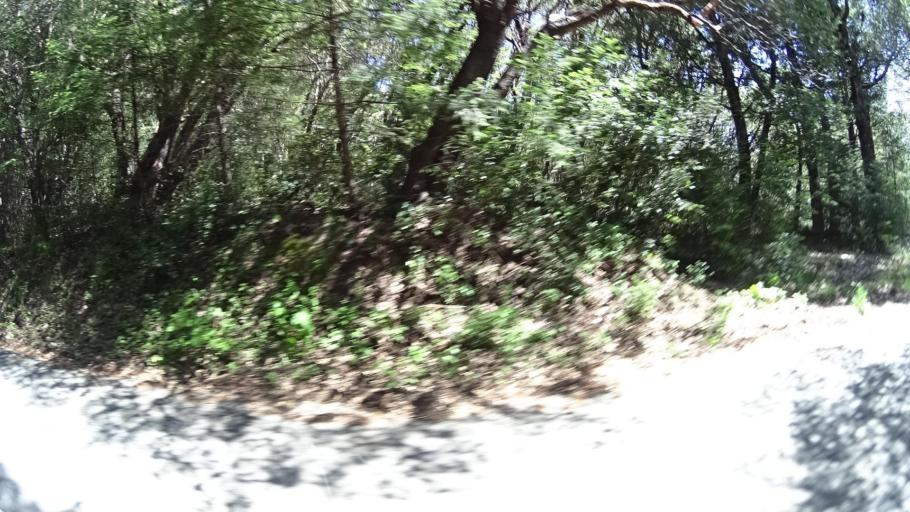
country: US
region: California
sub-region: Humboldt County
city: Redway
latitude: 40.1830
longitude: -124.0886
